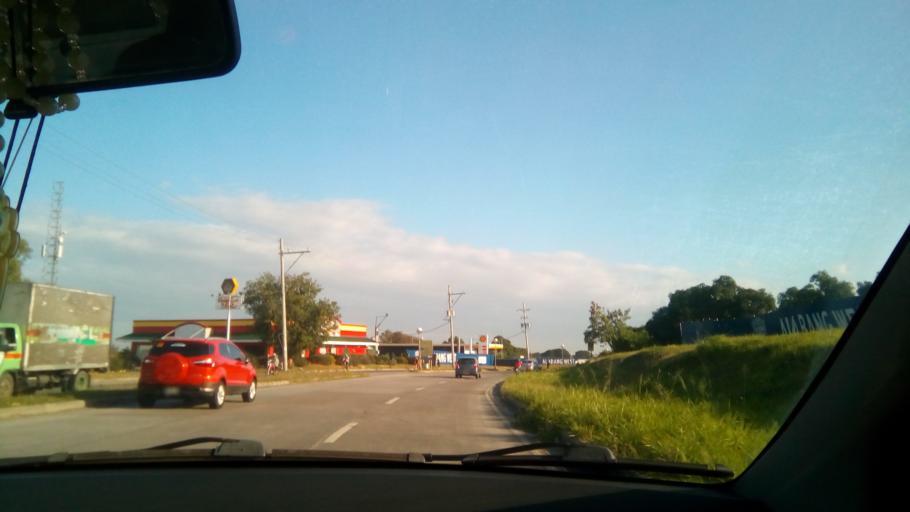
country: PH
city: Sambayanihan People's Village
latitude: 14.4061
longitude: 121.0119
